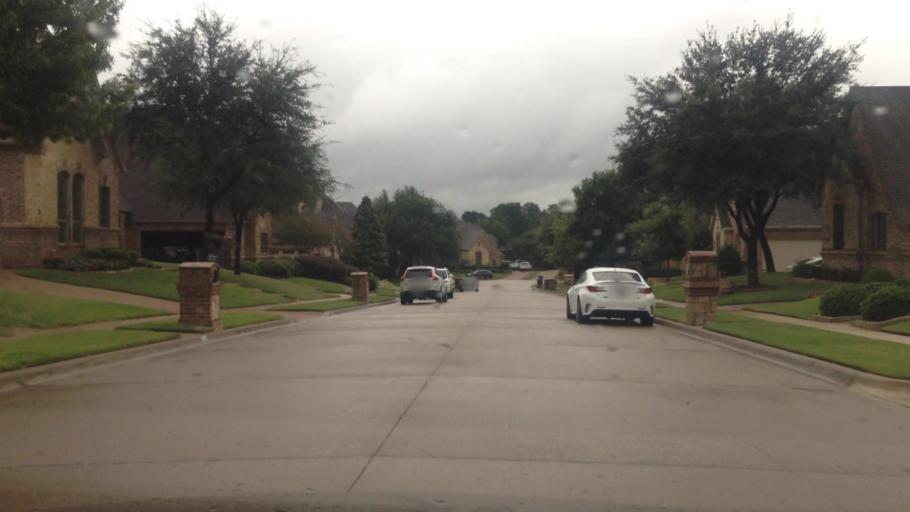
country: US
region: Texas
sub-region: Tarrant County
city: Colleyville
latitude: 32.8675
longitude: -97.1908
